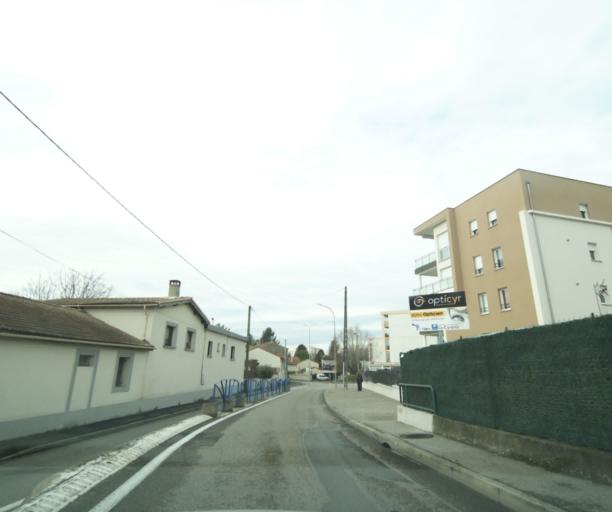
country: FR
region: Rhone-Alpes
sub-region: Departement de la Drome
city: Bourg-les-Valence
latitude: 44.9515
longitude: 4.9026
